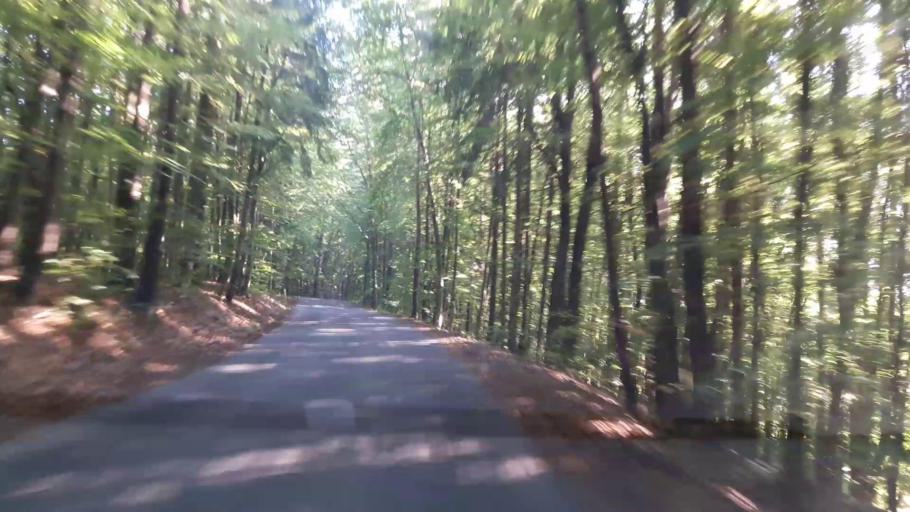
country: AT
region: Styria
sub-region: Politischer Bezirk Suedoststeiermark
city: Unterlamm
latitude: 46.9738
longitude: 16.0743
